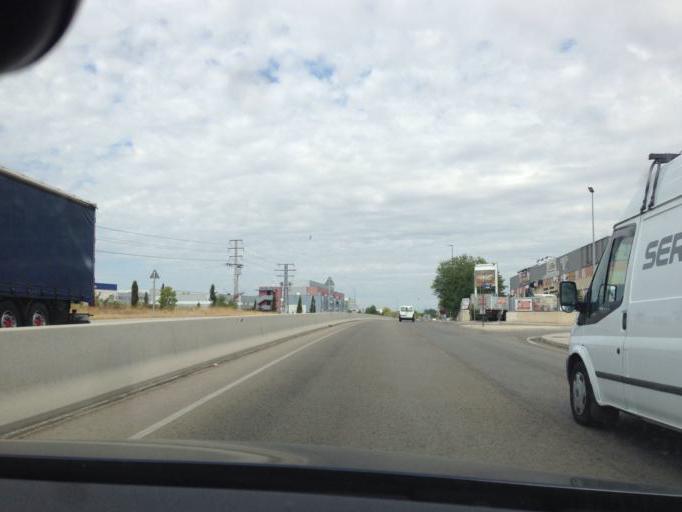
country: ES
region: Madrid
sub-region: Provincia de Madrid
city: Alcala de Henares
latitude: 40.4985
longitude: -3.3918
